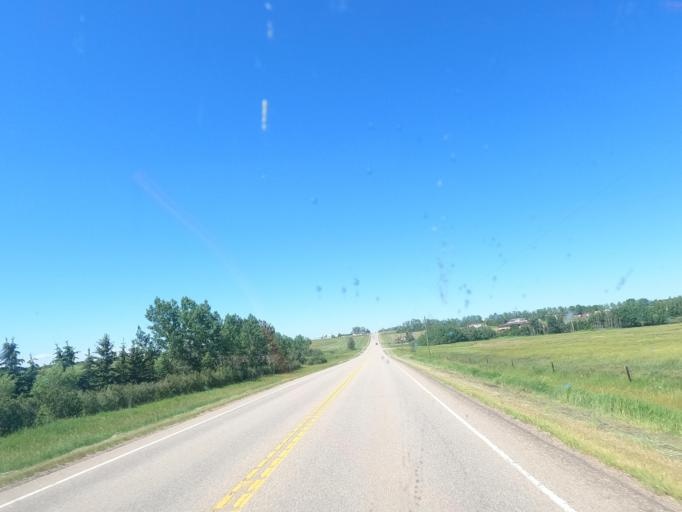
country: CA
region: Alberta
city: Chestermere
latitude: 51.1544
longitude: -113.7617
